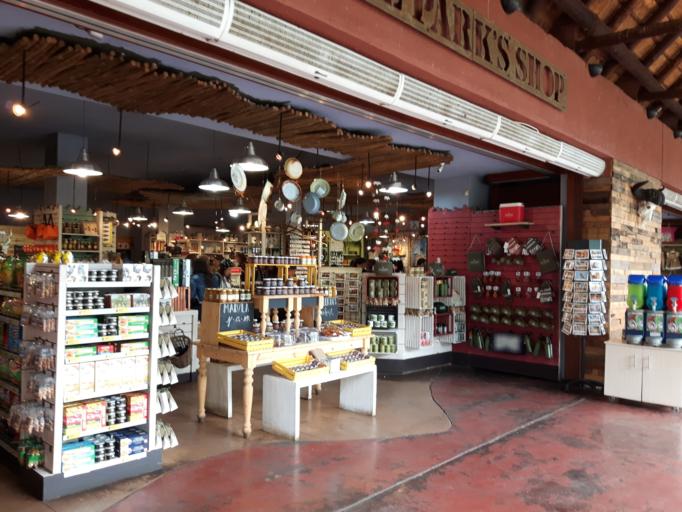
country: ZA
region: Mpumalanga
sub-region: Ehlanzeni District
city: Komatipoort
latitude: -25.1191
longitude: 31.9162
